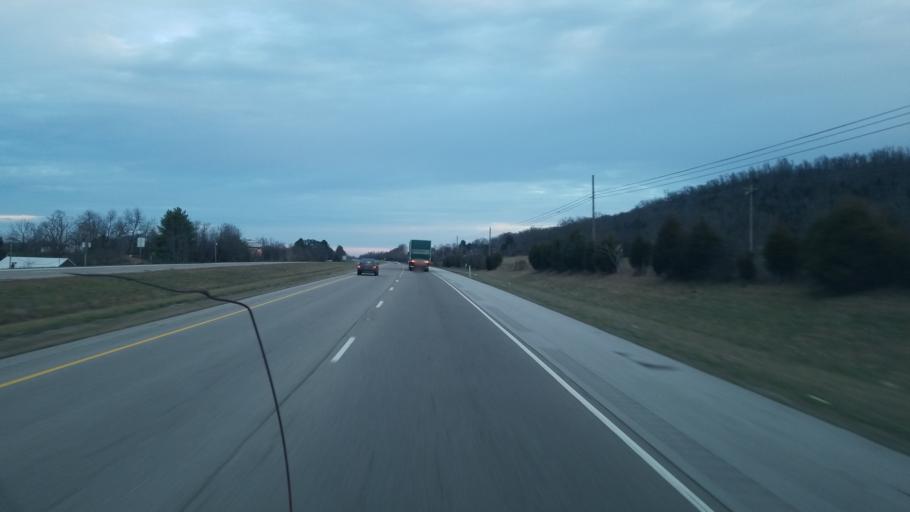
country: US
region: Tennessee
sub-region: White County
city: Sparta
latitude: 35.9992
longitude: -85.5031
